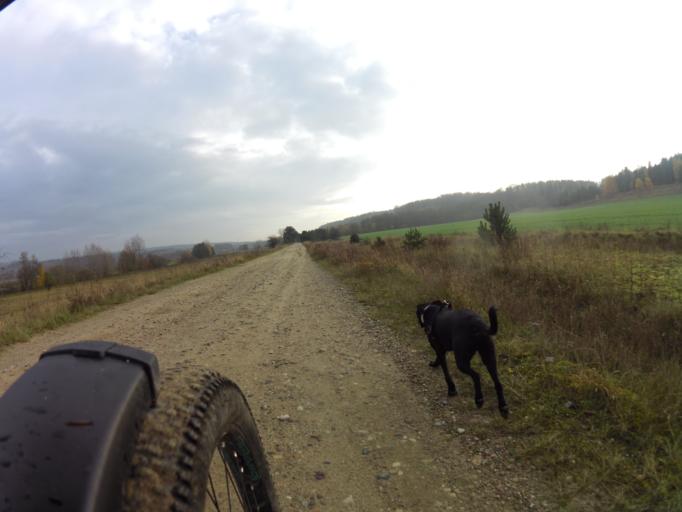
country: PL
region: Pomeranian Voivodeship
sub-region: Powiat wejherowski
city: Gniewino
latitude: 54.7073
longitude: 18.1016
